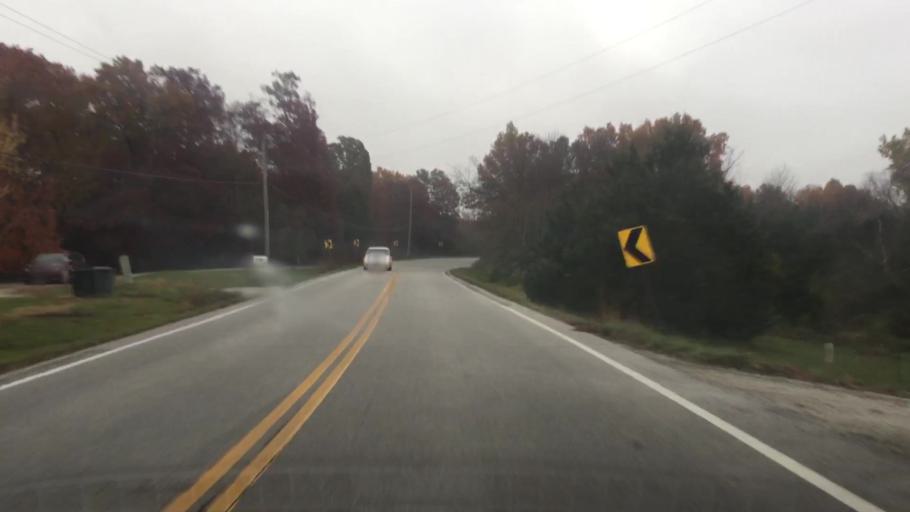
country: US
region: Missouri
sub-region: Callaway County
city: Fulton
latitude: 38.8779
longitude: -92.0827
